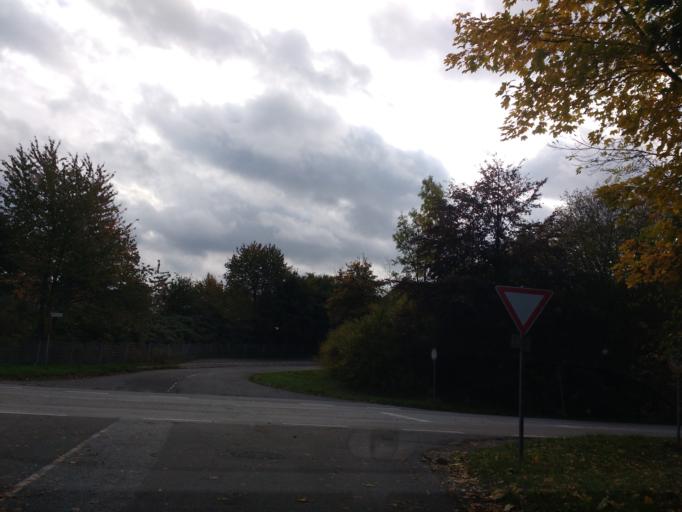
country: DE
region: Schleswig-Holstein
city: Travemuende
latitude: 53.9687
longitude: 10.8560
